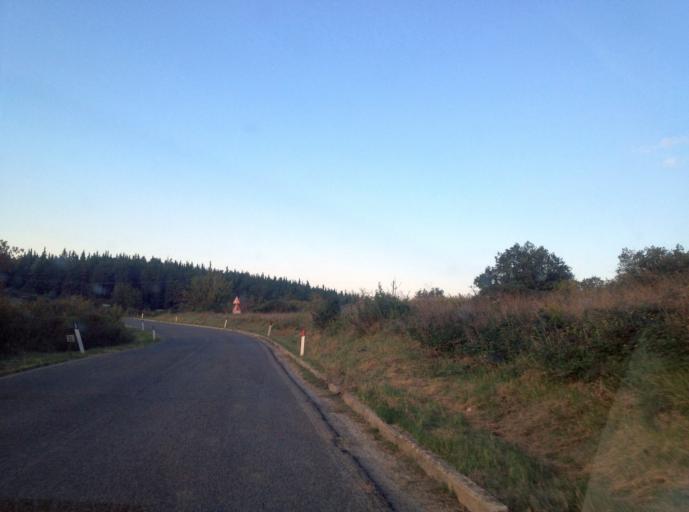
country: IT
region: Tuscany
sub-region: Provincia di Siena
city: Castellina in Chianti
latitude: 43.4450
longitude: 11.3000
